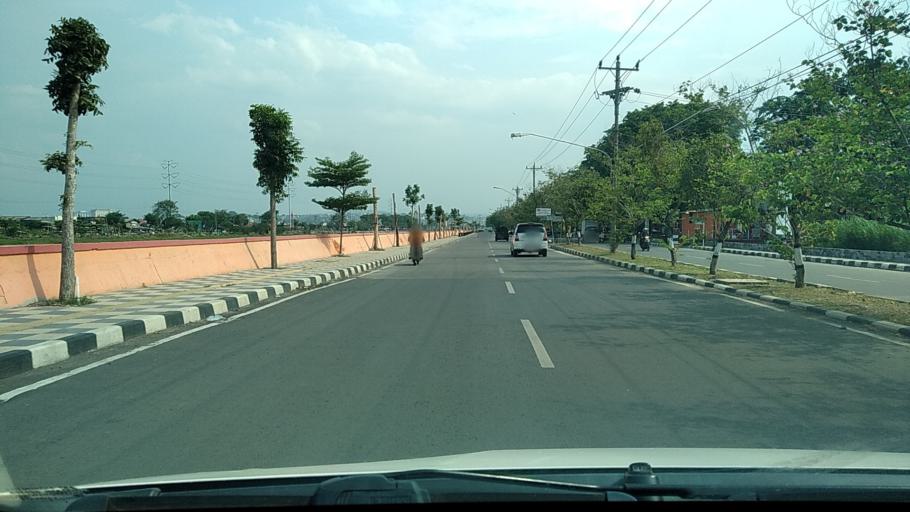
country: ID
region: Central Java
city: Semarang
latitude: -6.9686
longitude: 110.3999
